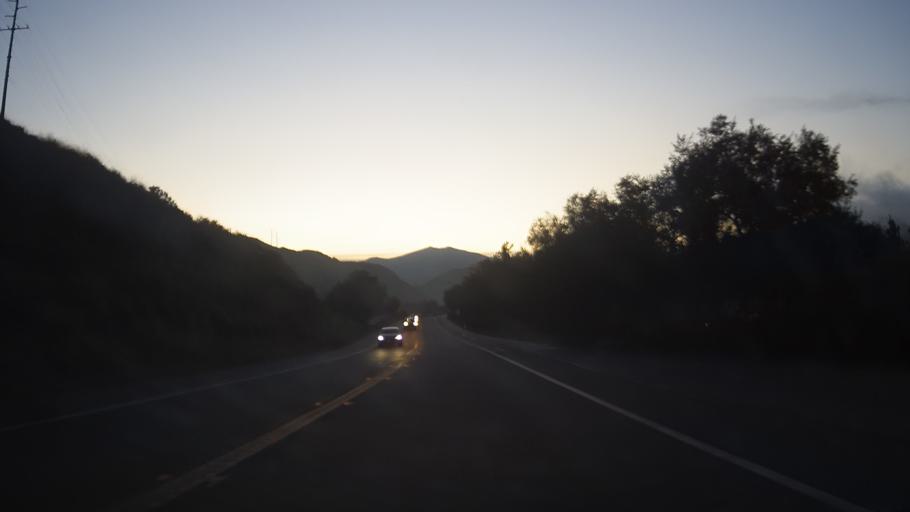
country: US
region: California
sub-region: San Diego County
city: Crest
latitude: 32.7853
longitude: -116.8826
